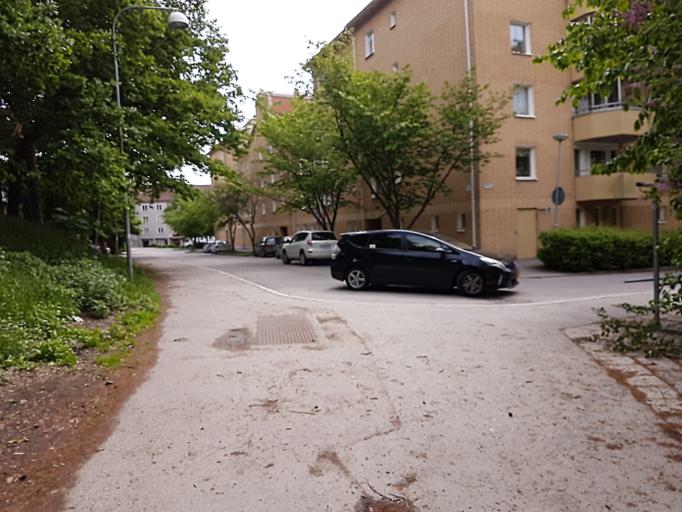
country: SE
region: Stockholm
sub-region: Solna Kommun
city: Rasunda
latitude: 59.3626
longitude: 17.9827
